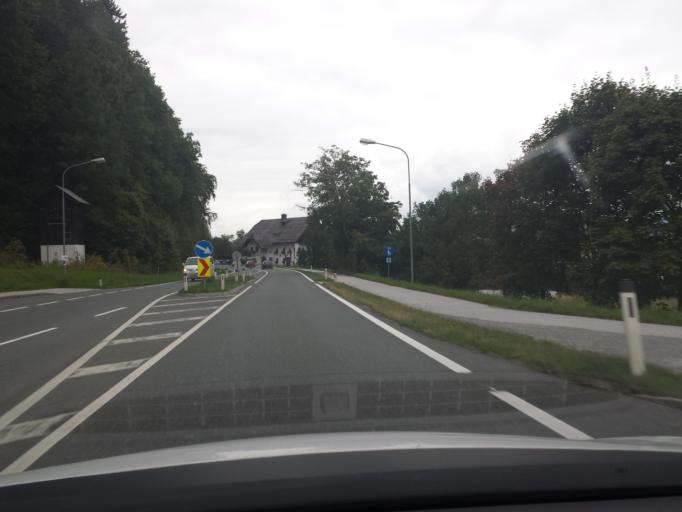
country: AT
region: Salzburg
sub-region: Politischer Bezirk Salzburg-Umgebung
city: Thalgau
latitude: 47.8088
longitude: 13.2470
